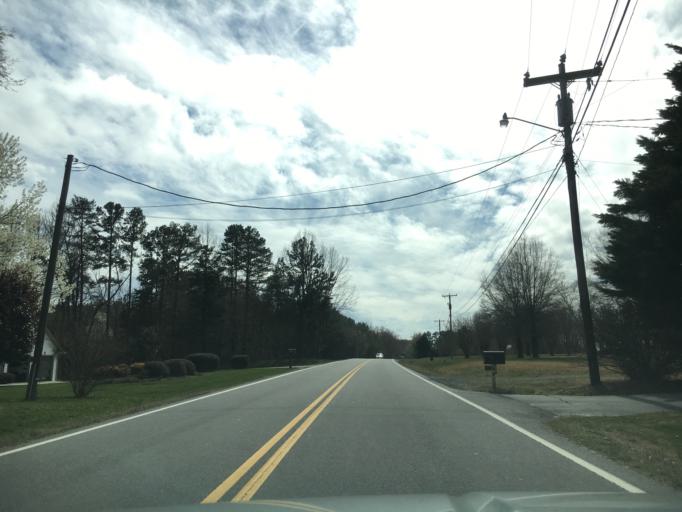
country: US
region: Virginia
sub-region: Halifax County
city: Halifax
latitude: 36.7535
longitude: -78.9180
